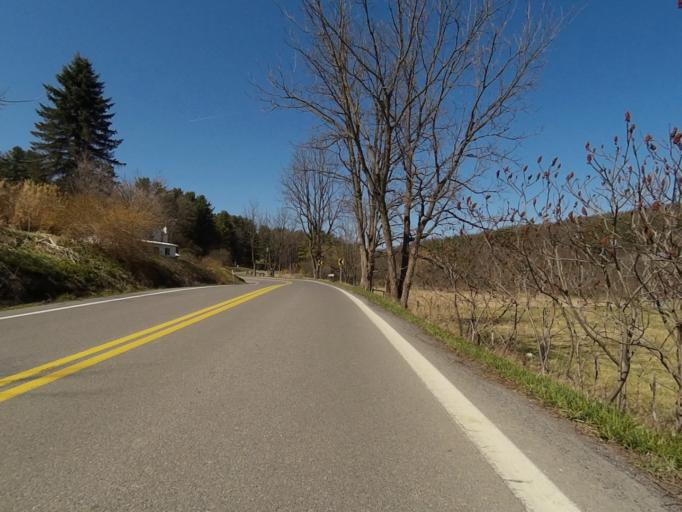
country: US
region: Pennsylvania
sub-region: Centre County
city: Stormstown
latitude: 40.7447
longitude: -78.0292
